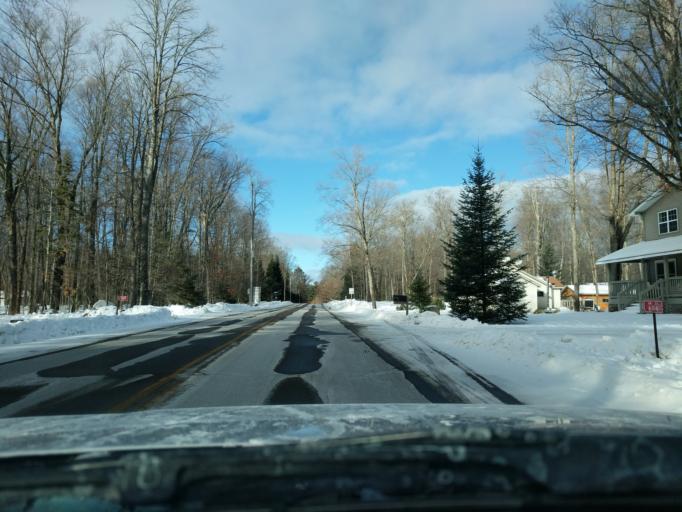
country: US
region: Wisconsin
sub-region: Vilas County
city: Eagle River
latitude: 45.7852
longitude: -89.0780
